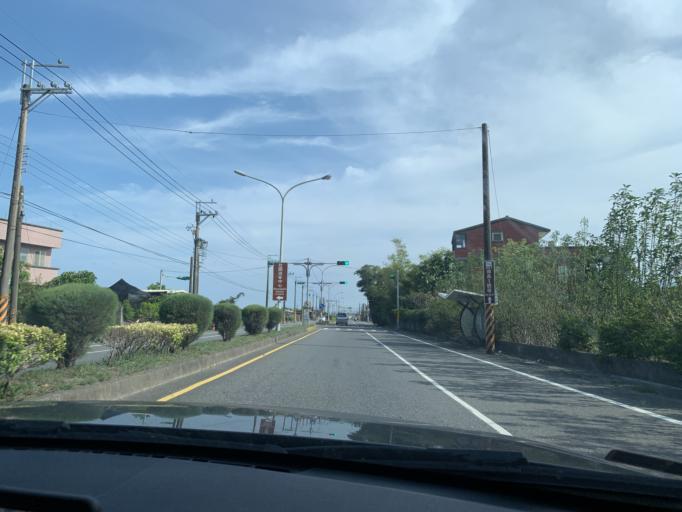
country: TW
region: Taiwan
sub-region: Yilan
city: Yilan
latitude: 24.7390
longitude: 121.8172
